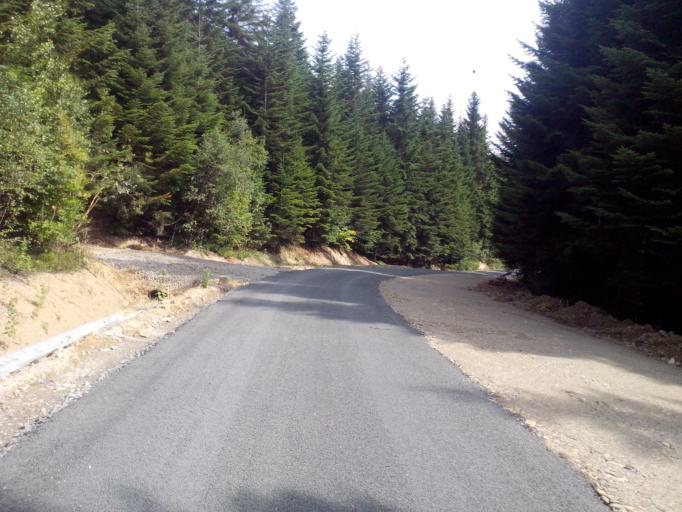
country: PL
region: Subcarpathian Voivodeship
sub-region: Powiat strzyzowski
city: Strzyzow
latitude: 49.8116
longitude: 21.8005
